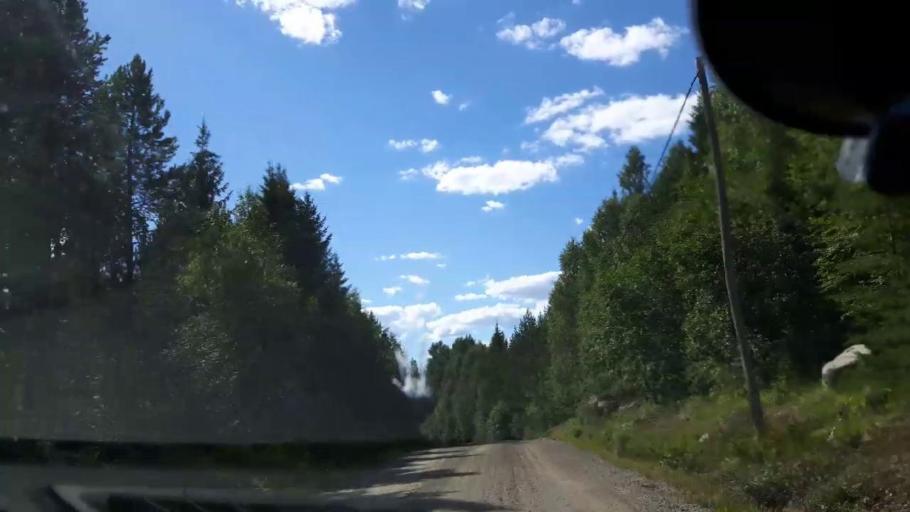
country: SE
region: Vaesternorrland
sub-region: Ange Kommun
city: Fransta
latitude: 62.7884
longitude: 16.1282
